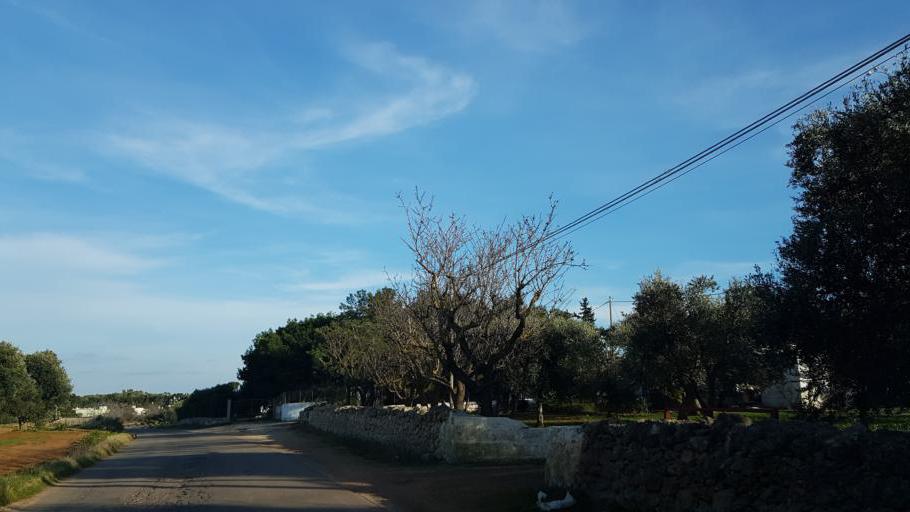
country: IT
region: Apulia
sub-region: Provincia di Brindisi
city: San Vito dei Normanni
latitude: 40.6954
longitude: 17.7525
